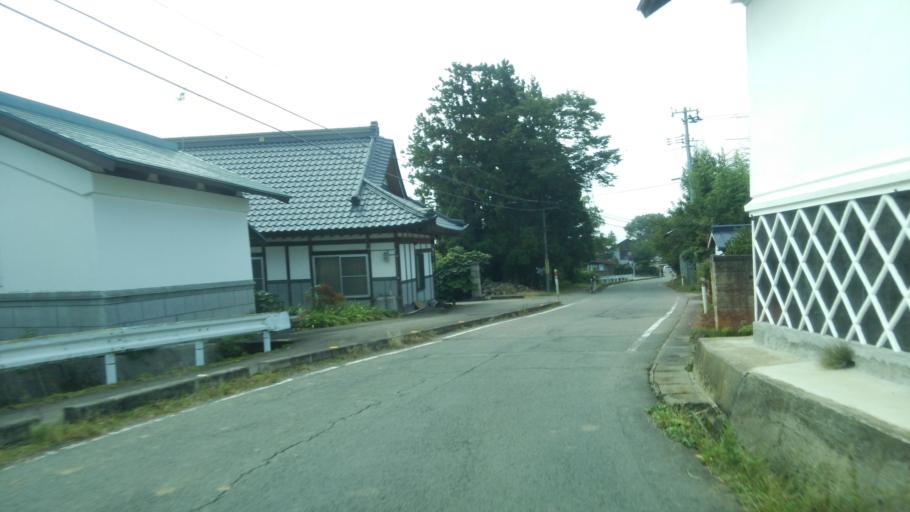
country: JP
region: Fukushima
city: Kitakata
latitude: 37.5801
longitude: 139.9465
